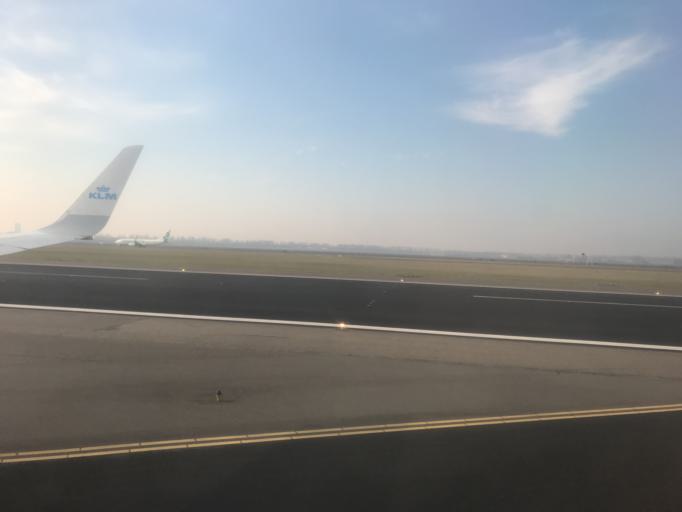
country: NL
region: North Holland
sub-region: Gemeente Haarlemmermeer
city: Hoofddorp
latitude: 52.3123
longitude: 4.7385
